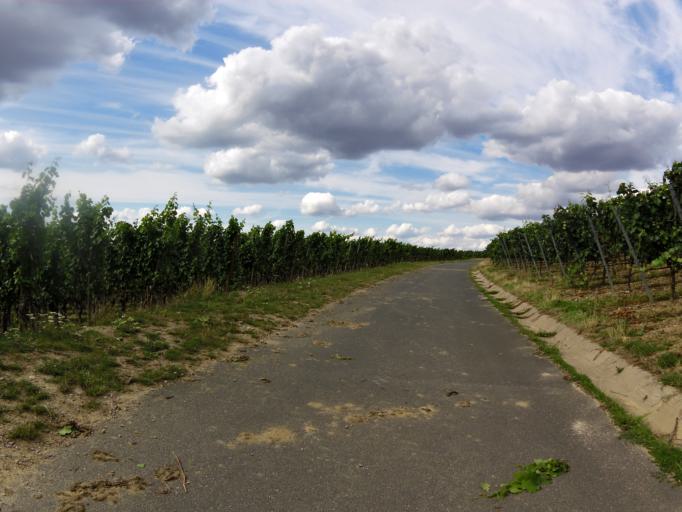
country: DE
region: Bavaria
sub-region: Regierungsbezirk Unterfranken
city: Sommerhausen
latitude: 49.6907
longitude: 10.0311
